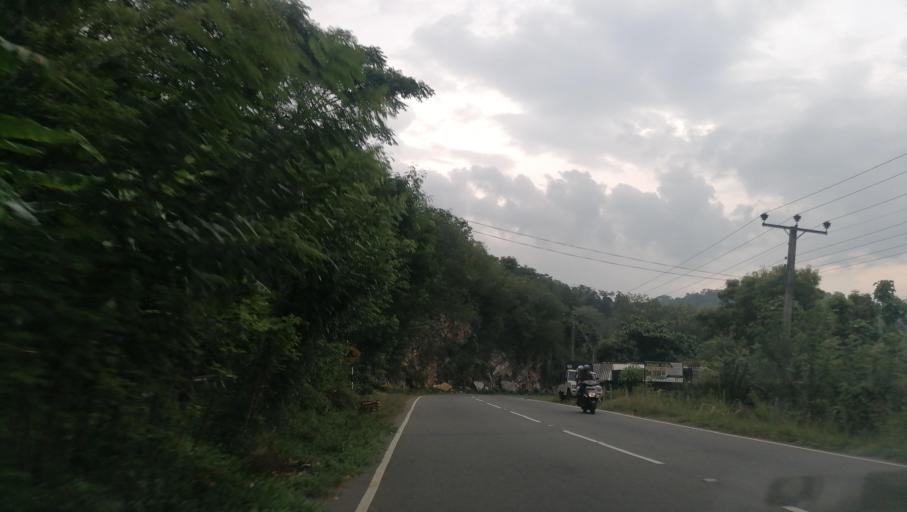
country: LK
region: Central
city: Kandy
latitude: 7.2219
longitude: 80.7630
